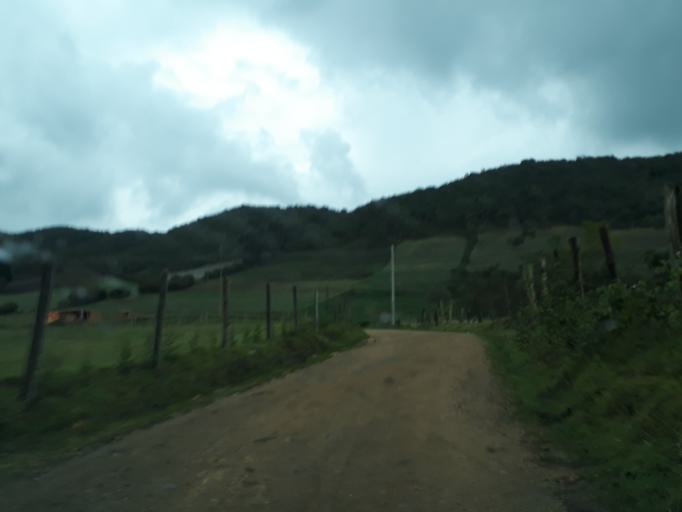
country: CO
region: Cundinamarca
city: Lenguazaque
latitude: 5.2769
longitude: -73.6420
